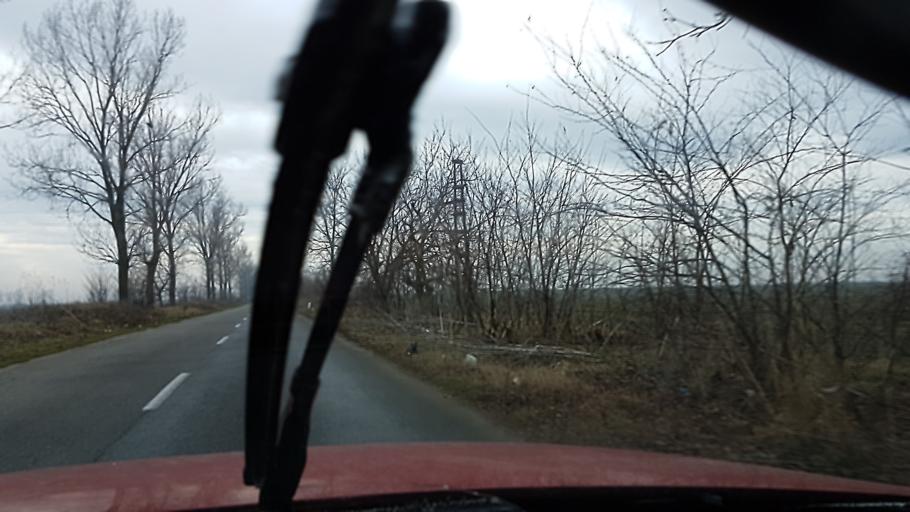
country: RO
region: Giurgiu
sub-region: Comuna Herasti
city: Herasti
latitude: 44.2492
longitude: 26.3679
